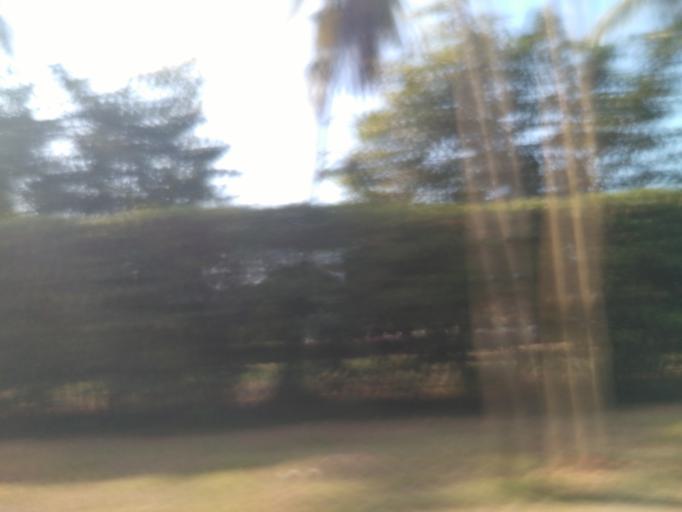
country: TZ
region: Dar es Salaam
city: Magomeni
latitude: -6.7742
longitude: 39.2811
